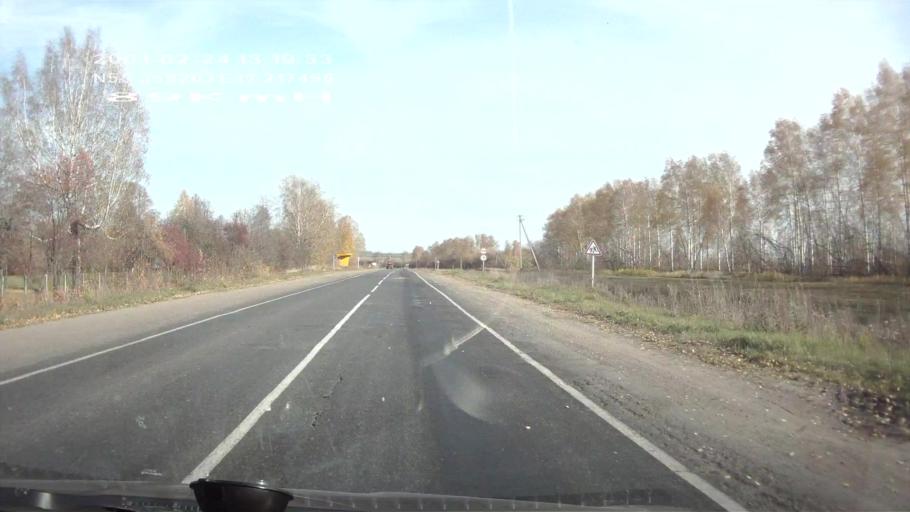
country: RU
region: Chuvashia
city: Ibresi
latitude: 55.3552
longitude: 47.2175
